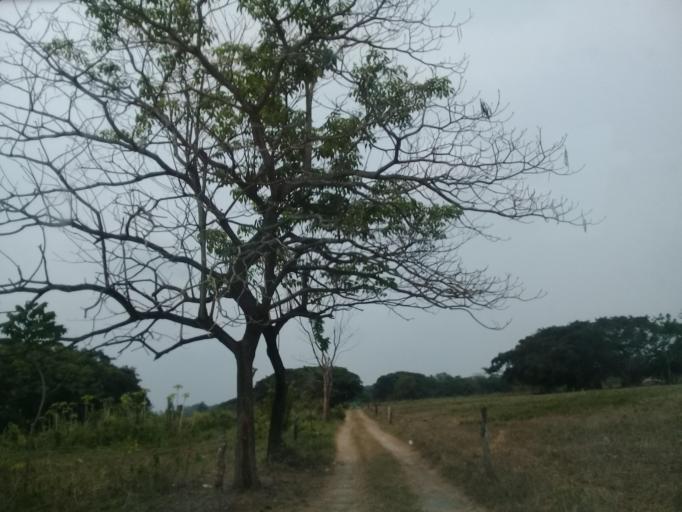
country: MX
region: Veracruz
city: El Tejar
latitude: 19.0454
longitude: -96.1904
